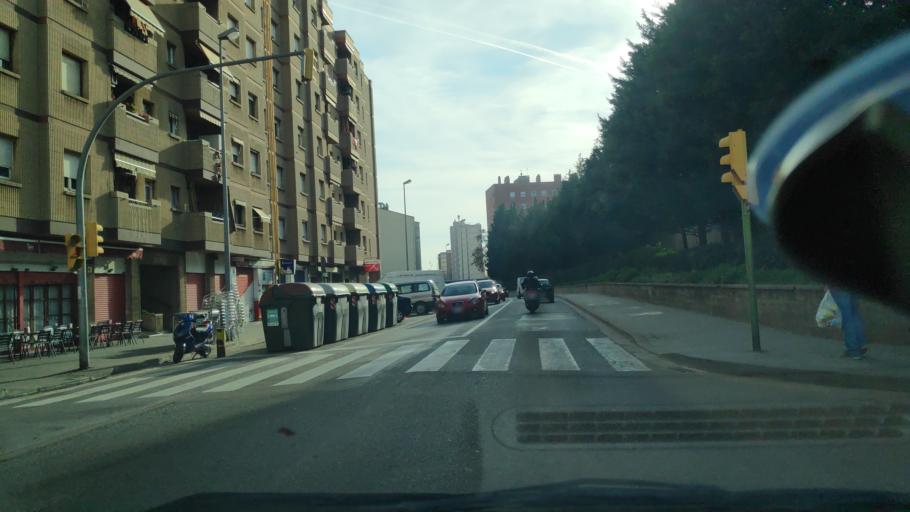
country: ES
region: Catalonia
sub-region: Provincia de Barcelona
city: Sabadell
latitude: 41.5635
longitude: 2.1009
